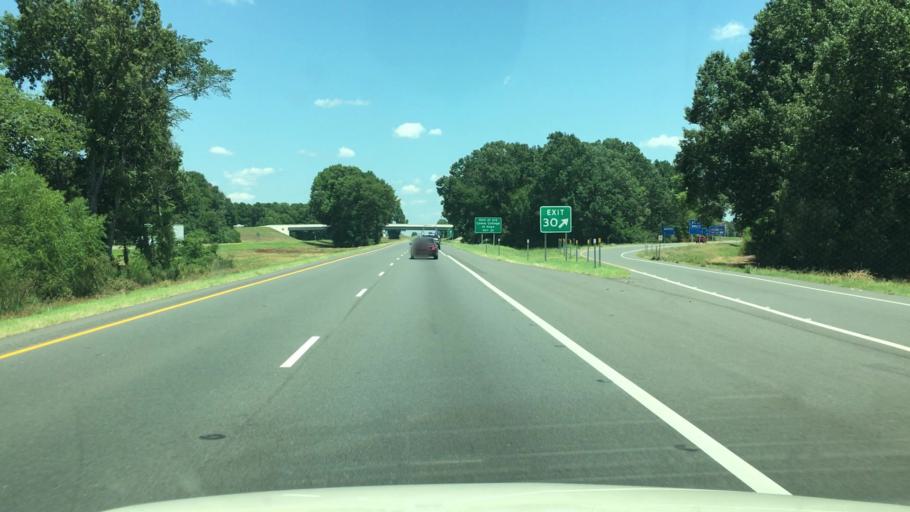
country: US
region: Arkansas
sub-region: Hempstead County
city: Hope
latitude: 33.6792
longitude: -93.6139
